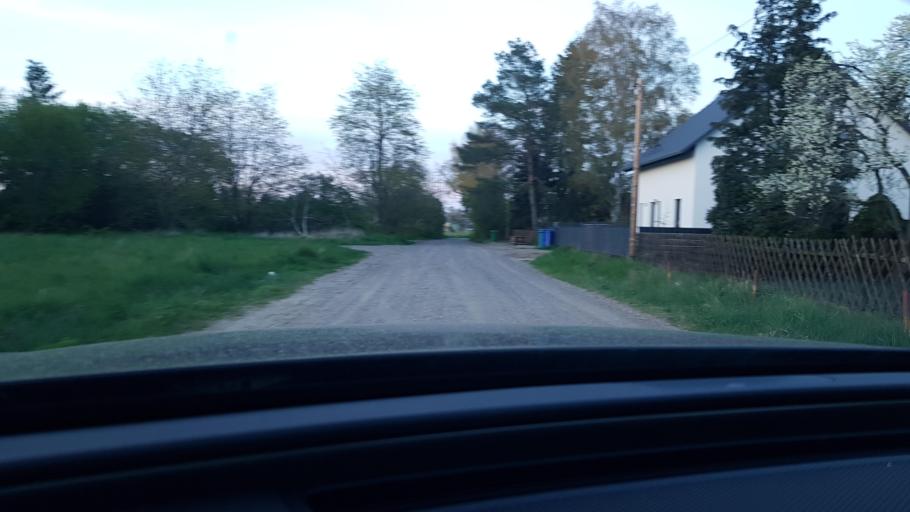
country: DE
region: Berlin
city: Lichtenrade
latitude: 52.3522
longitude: 13.4227
